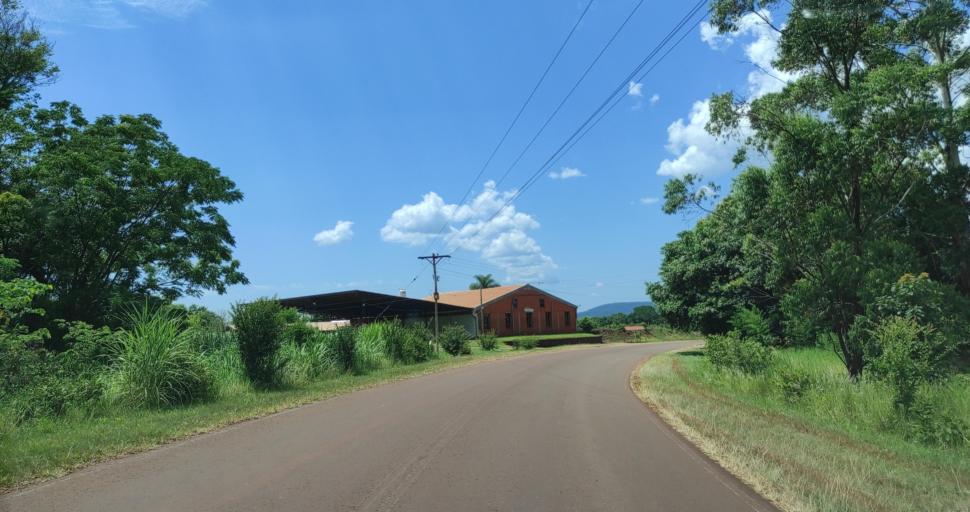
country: AR
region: Misiones
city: Ruiz de Montoya
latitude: -27.0232
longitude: -55.0327
